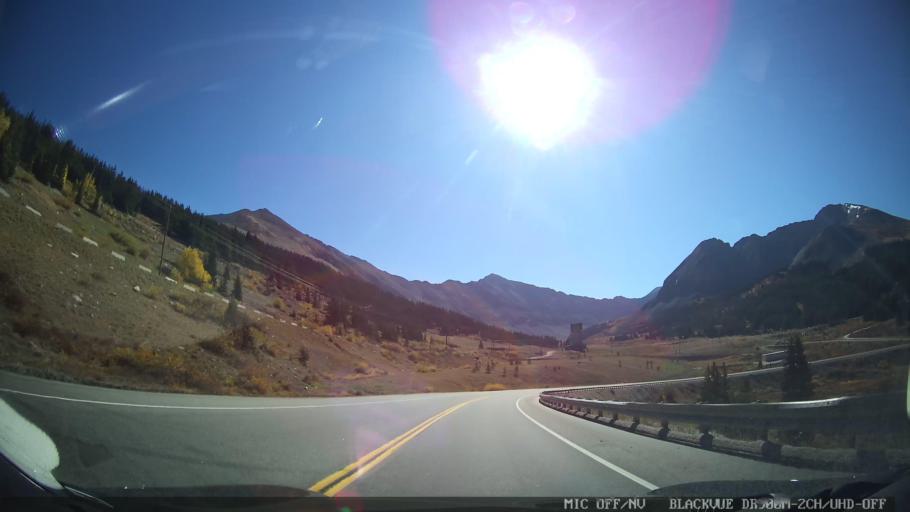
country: US
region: Colorado
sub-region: Lake County
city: Leadville
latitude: 39.3647
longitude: -106.1752
